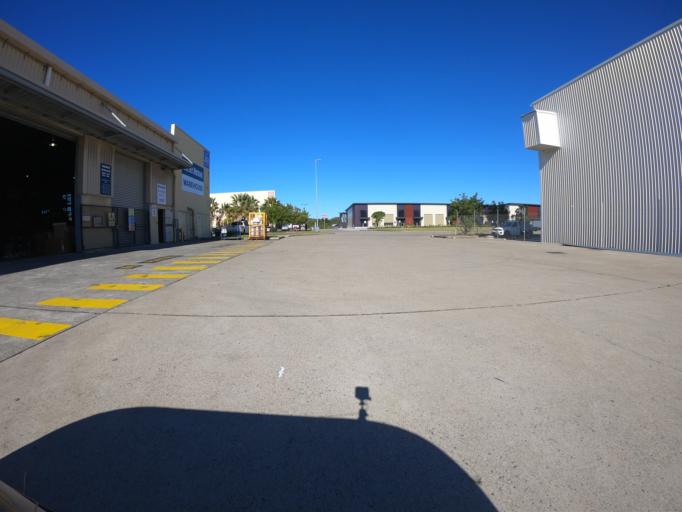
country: AU
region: New South Wales
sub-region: Wollongong
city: Port Kembla
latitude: -34.4970
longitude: 150.8934
